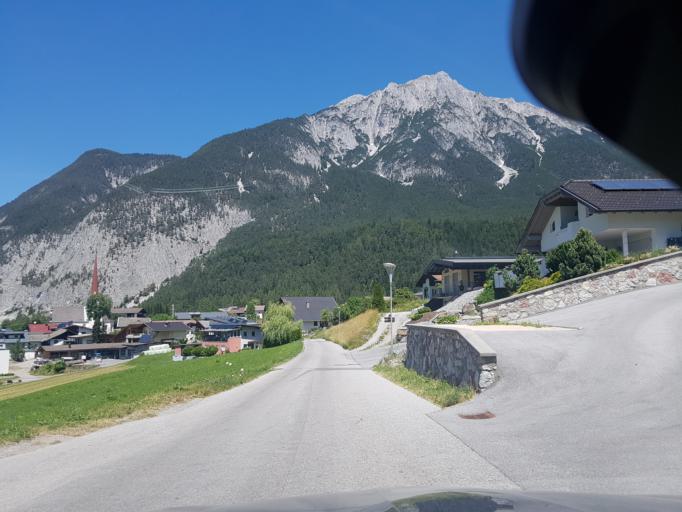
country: AT
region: Tyrol
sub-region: Politischer Bezirk Imst
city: Nassereith
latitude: 47.3053
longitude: 10.8531
